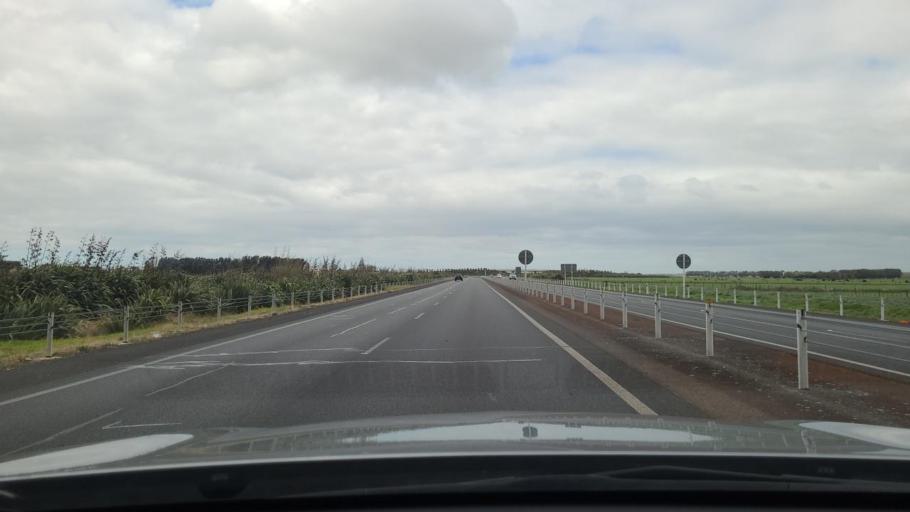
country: NZ
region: Bay of Plenty
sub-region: Tauranga City
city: Tauranga
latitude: -37.7190
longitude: 176.2969
